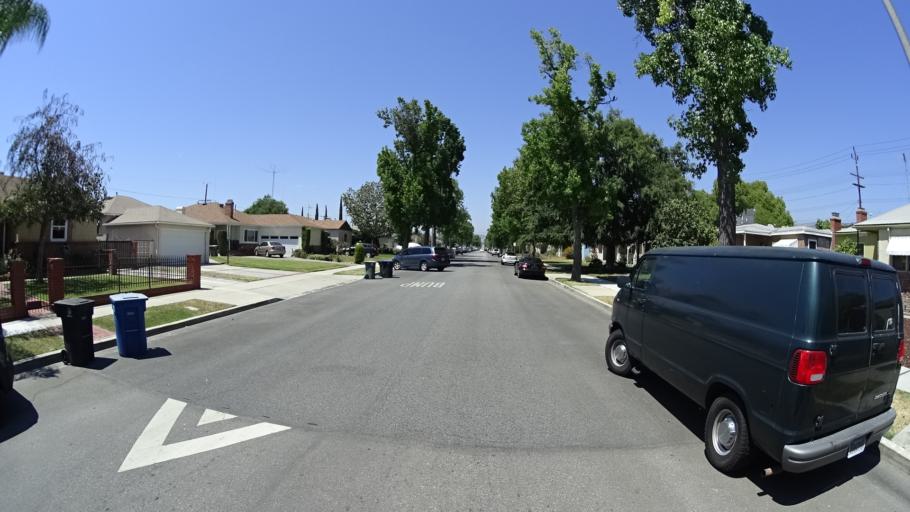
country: US
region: California
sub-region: Los Angeles County
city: North Hollywood
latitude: 34.1782
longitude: -118.3505
